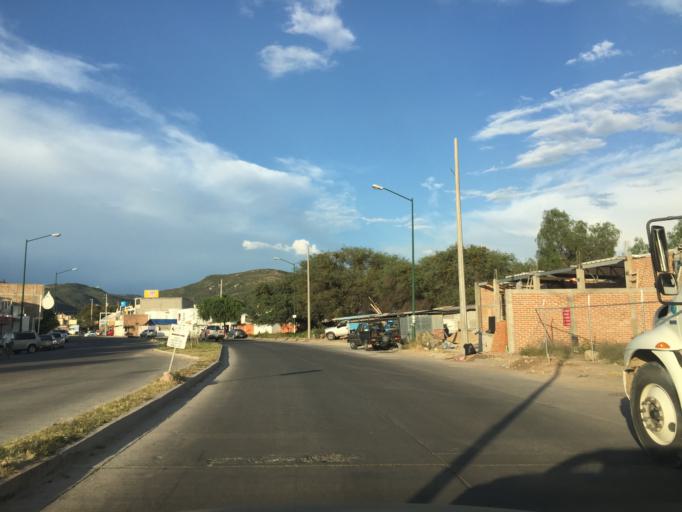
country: MX
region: Guanajuato
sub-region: Leon
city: Medina
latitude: 21.1710
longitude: -101.6506
